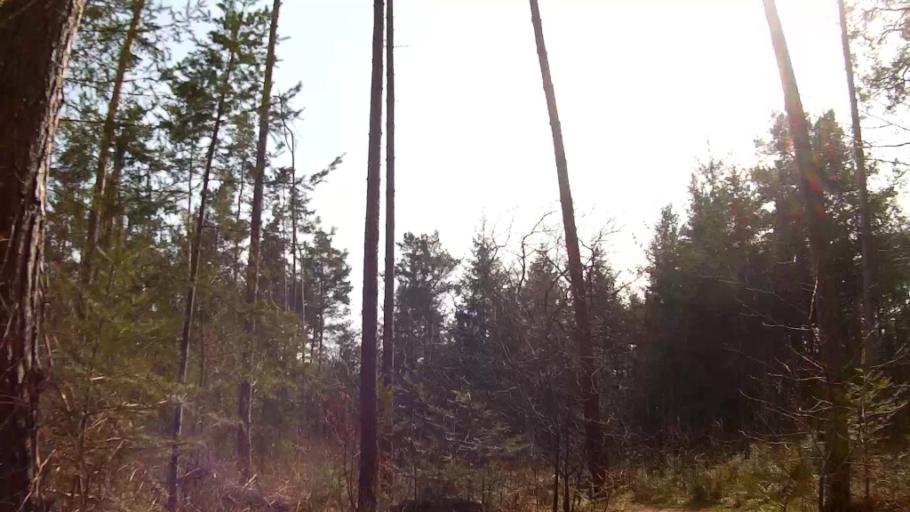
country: NL
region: Utrecht
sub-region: Gemeente Baarn
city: Baarn
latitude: 52.1883
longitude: 5.2378
